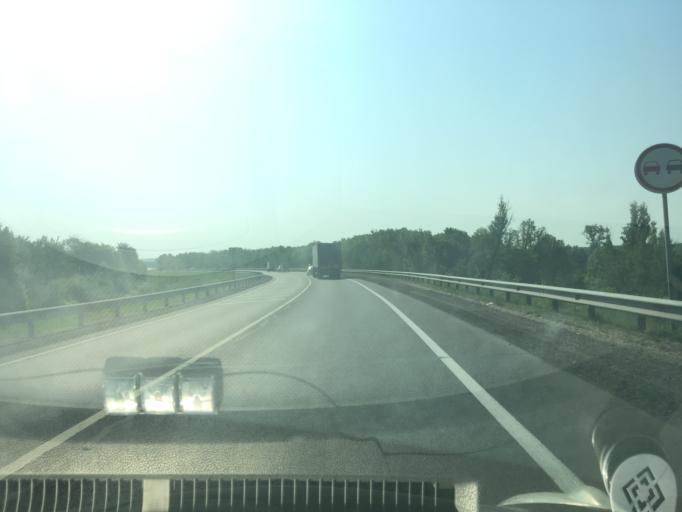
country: RU
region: Nizjnij Novgorod
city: Kstovo
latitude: 56.0965
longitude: 44.3119
